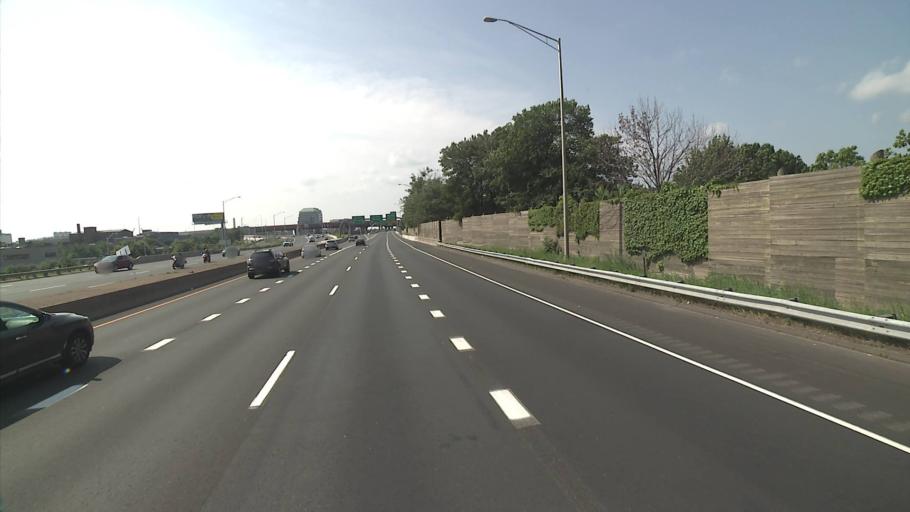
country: US
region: Connecticut
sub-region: New Haven County
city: New Haven
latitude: 41.3063
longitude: -72.9144
